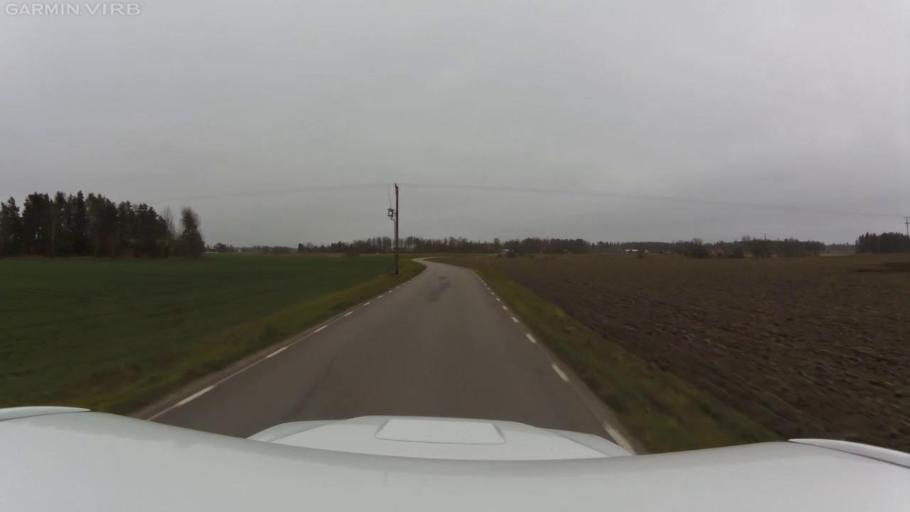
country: SE
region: OEstergoetland
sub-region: Linkopings Kommun
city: Vikingstad
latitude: 58.3192
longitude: 15.3762
